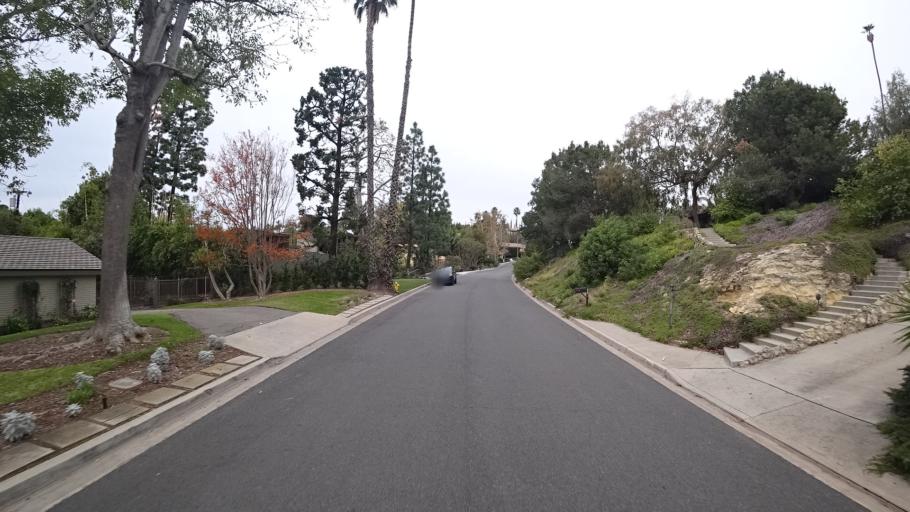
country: US
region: California
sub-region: Orange County
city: North Tustin
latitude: 33.7551
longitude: -117.7846
